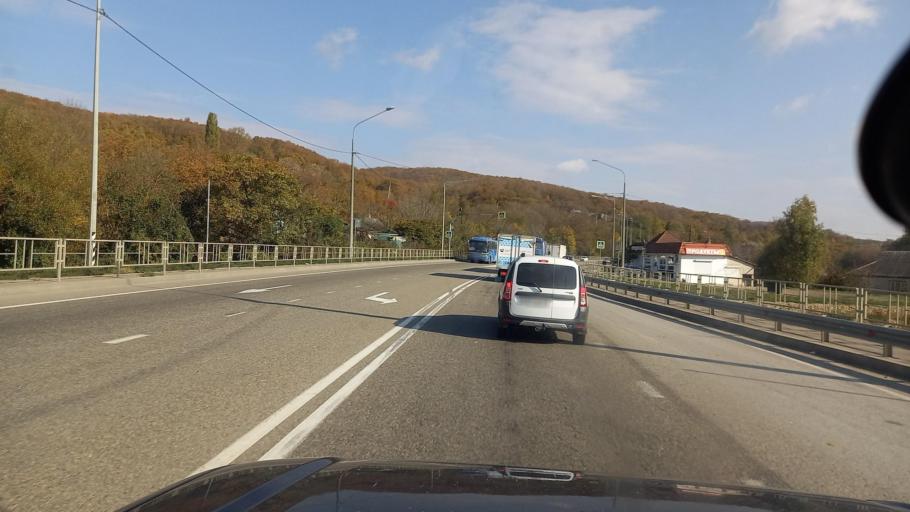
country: RU
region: Krasnodarskiy
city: Verkhnebakanskiy
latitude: 44.8674
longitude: 37.7459
